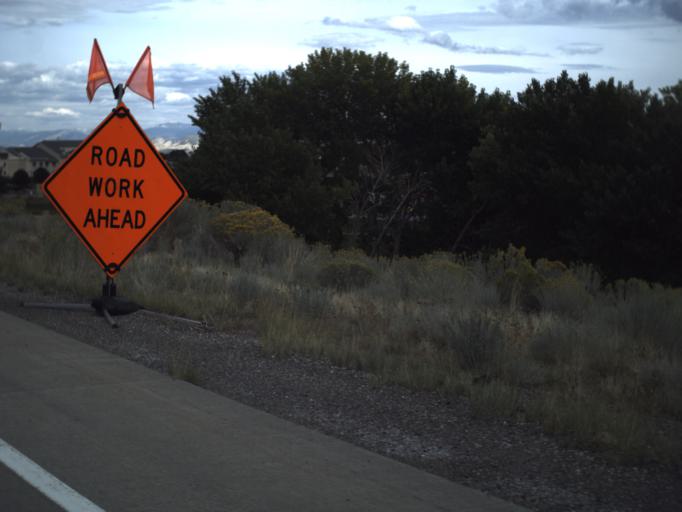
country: US
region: Utah
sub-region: Sevier County
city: Richfield
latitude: 38.7467
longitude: -112.1071
